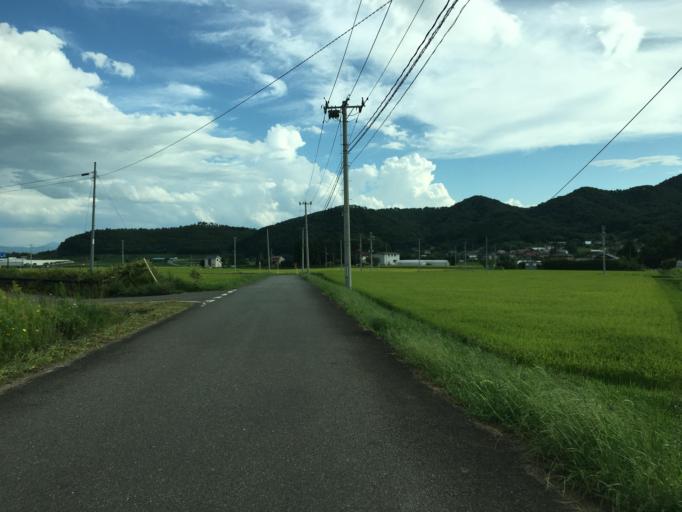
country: JP
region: Fukushima
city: Motomiya
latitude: 37.5265
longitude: 140.3704
